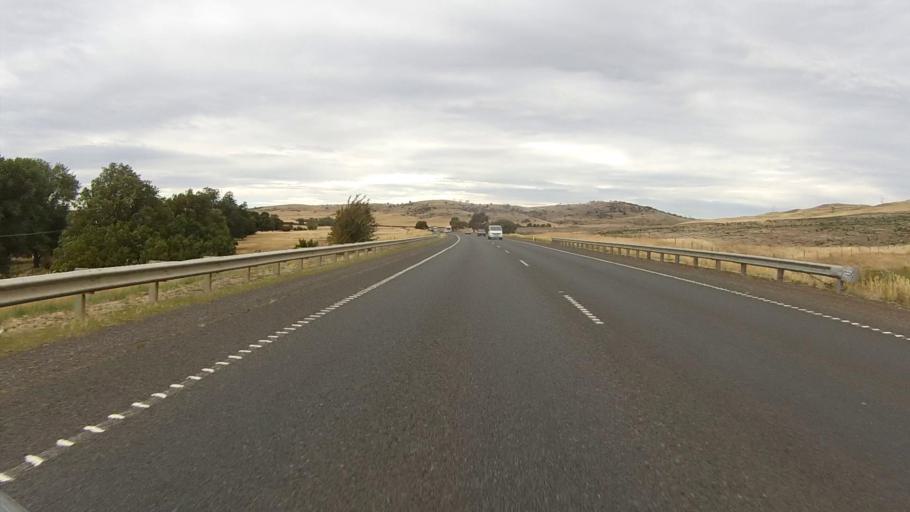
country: AU
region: Tasmania
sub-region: Brighton
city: Bridgewater
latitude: -42.3752
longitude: 147.3281
